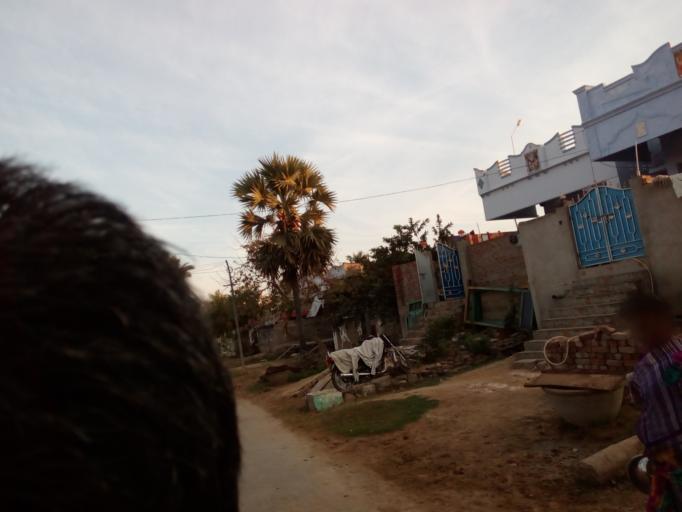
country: IN
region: Andhra Pradesh
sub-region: Prakasam
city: Vetapalem
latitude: 15.7254
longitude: 80.2551
